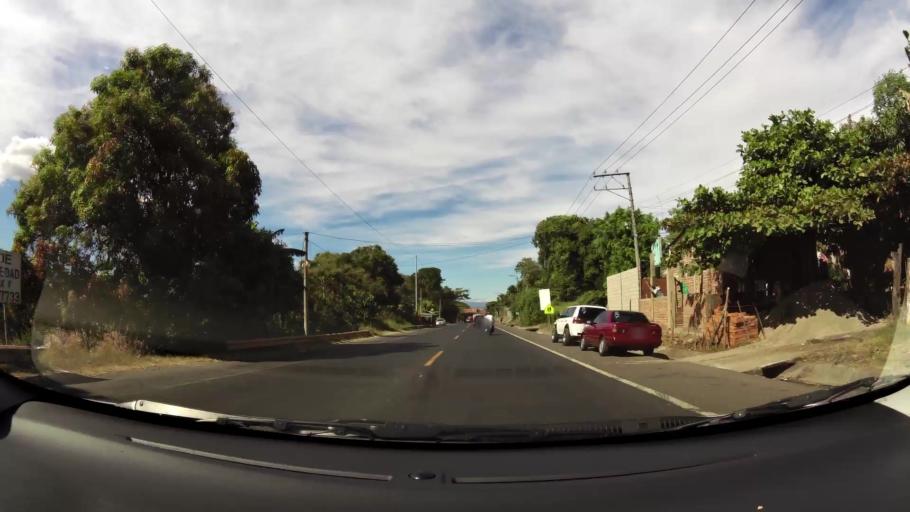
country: SV
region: San Salvador
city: Aguilares
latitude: 13.9205
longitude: -89.1840
